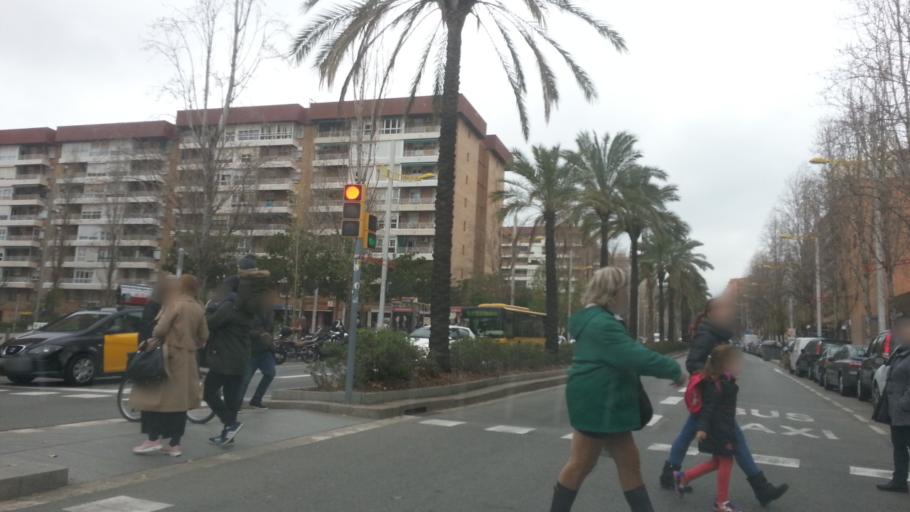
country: ES
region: Catalonia
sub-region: Provincia de Barcelona
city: Nou Barris
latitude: 41.4385
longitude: 2.1742
